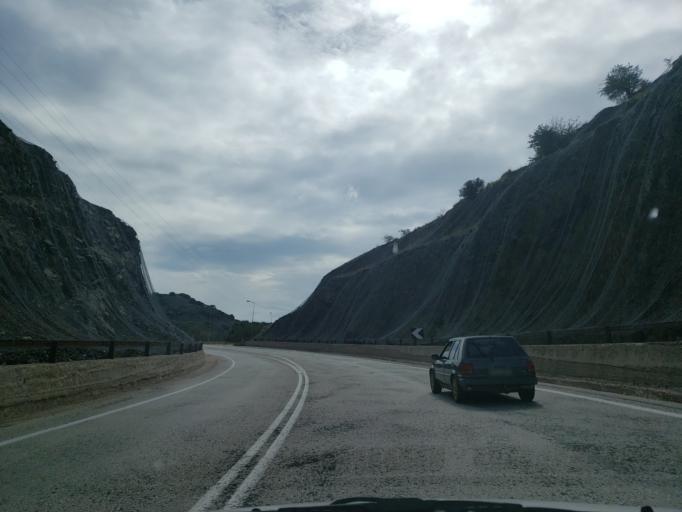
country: GR
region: Central Greece
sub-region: Nomos Fthiotidos
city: Stavros
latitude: 38.9900
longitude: 22.3727
